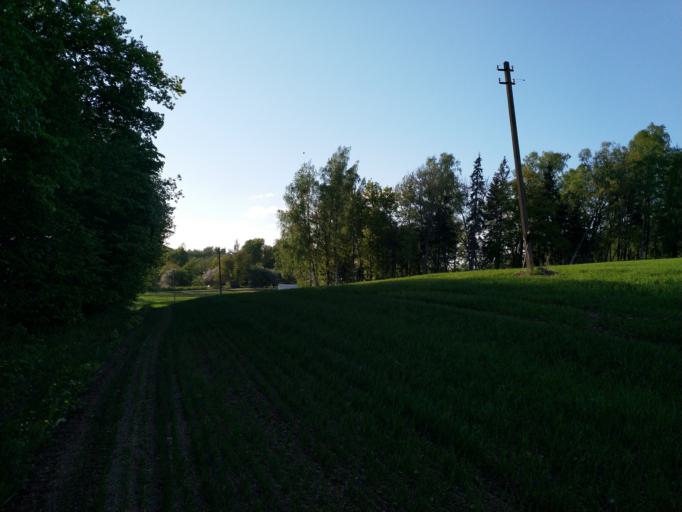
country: LV
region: Kuldigas Rajons
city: Kuldiga
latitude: 56.8620
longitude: 21.8560
